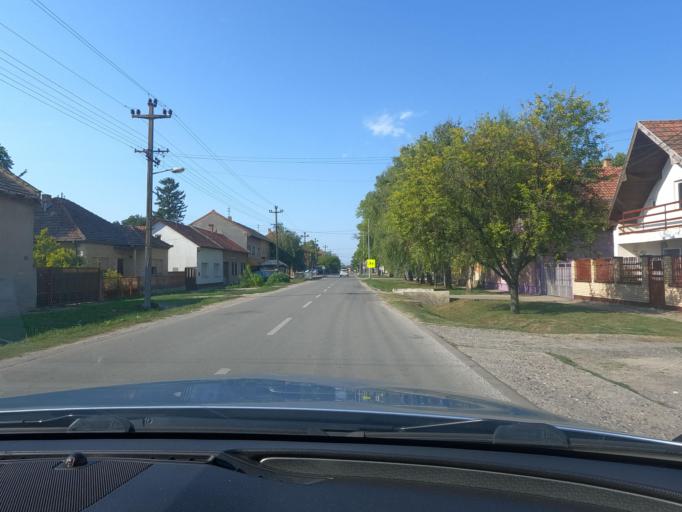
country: RS
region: Autonomna Pokrajina Vojvodina
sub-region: Juznobacki Okrug
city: Kovilj
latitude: 45.2236
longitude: 20.0207
